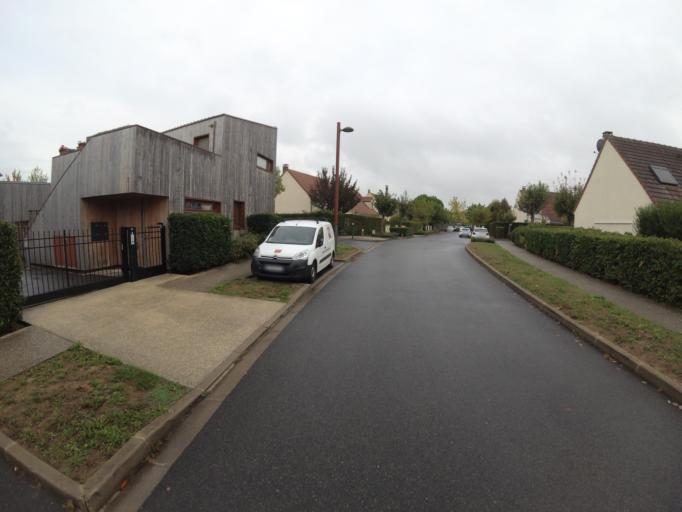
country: FR
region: Ile-de-France
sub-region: Departement de Seine-et-Marne
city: Chanteloup-en-Brie
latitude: 48.8571
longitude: 2.7440
